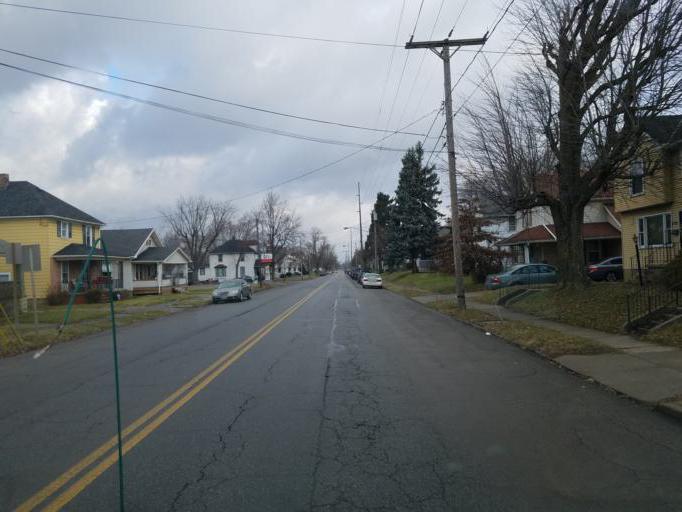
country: US
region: Ohio
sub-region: Marion County
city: Marion
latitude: 40.5751
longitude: -83.1433
